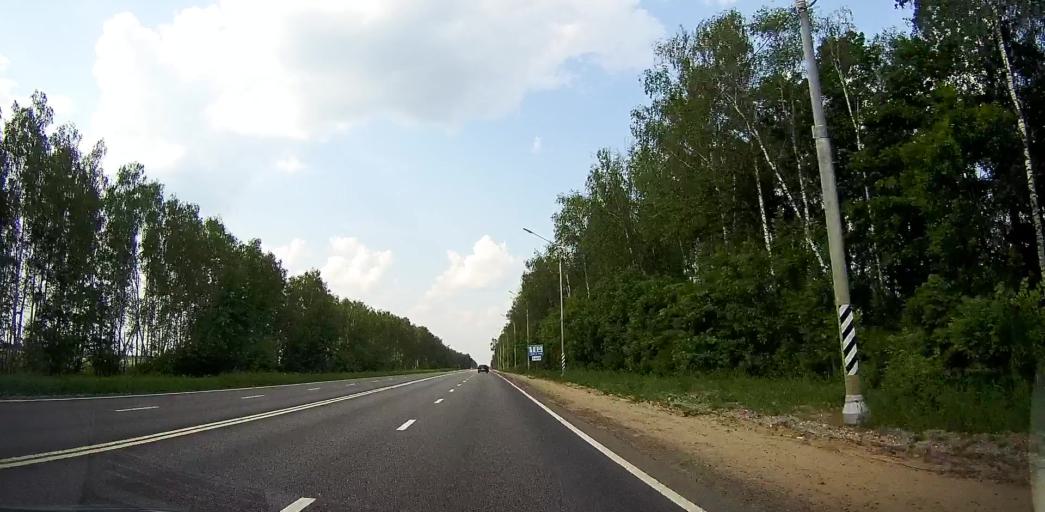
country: RU
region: Moskovskaya
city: Mikhnevo
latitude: 55.0974
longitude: 37.9500
